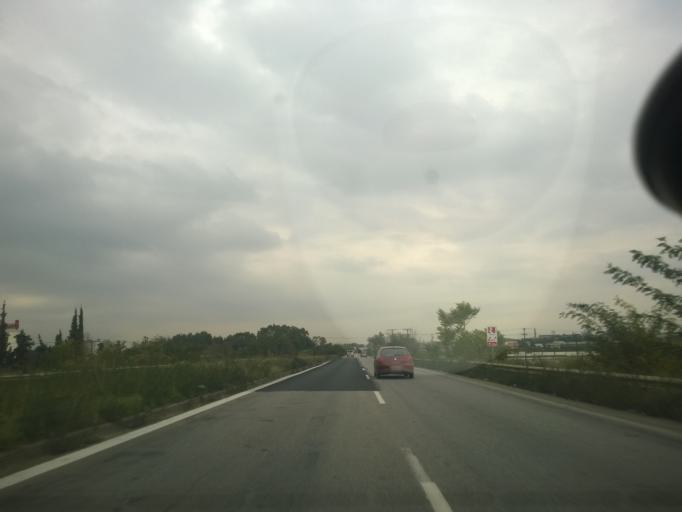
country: GR
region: Central Macedonia
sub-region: Nomos Thessalonikis
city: Nea Magnisia
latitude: 40.7001
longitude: 22.8305
